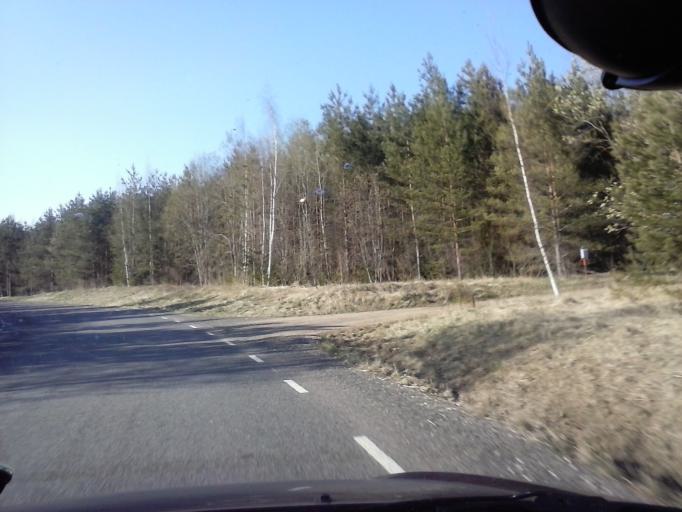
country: EE
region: Tartu
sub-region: UElenurme vald
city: Ulenurme
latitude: 58.1636
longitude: 26.8480
